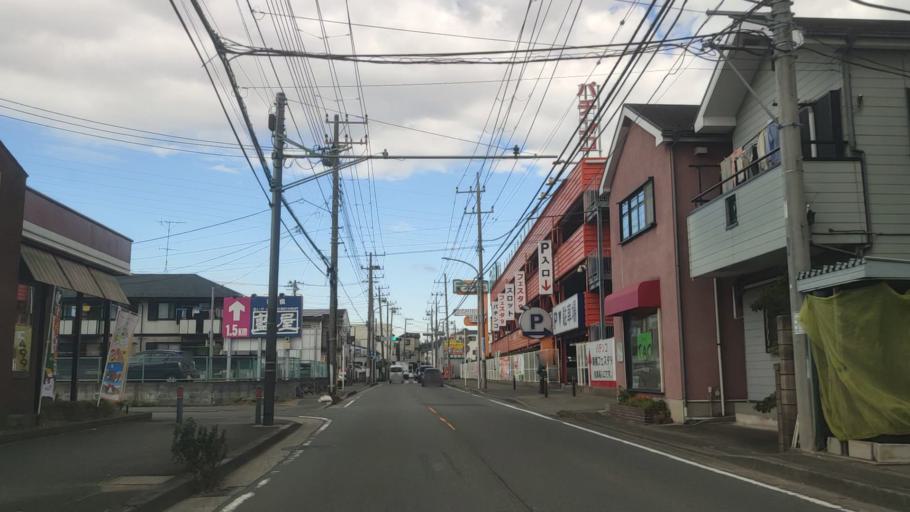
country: JP
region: Kanagawa
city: Minami-rinkan
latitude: 35.4238
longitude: 139.5311
